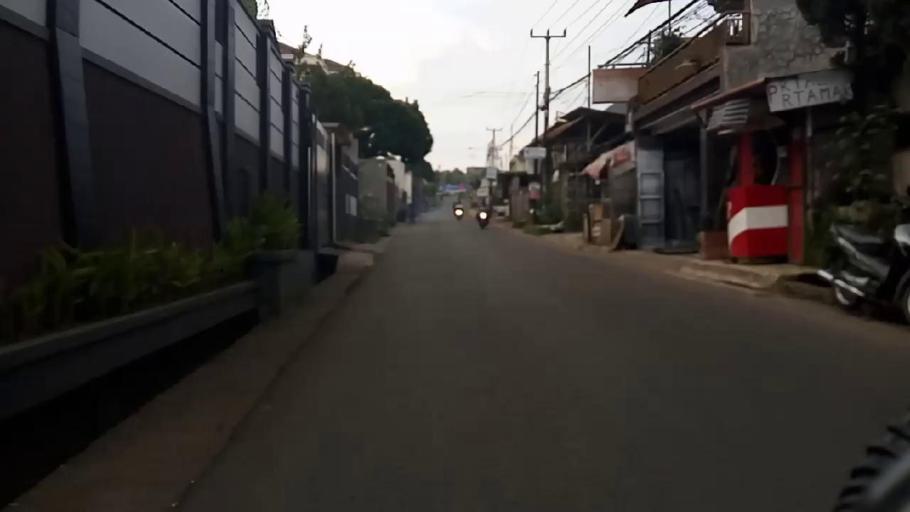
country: ID
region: West Java
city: Cimahi
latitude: -6.8614
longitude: 107.5765
